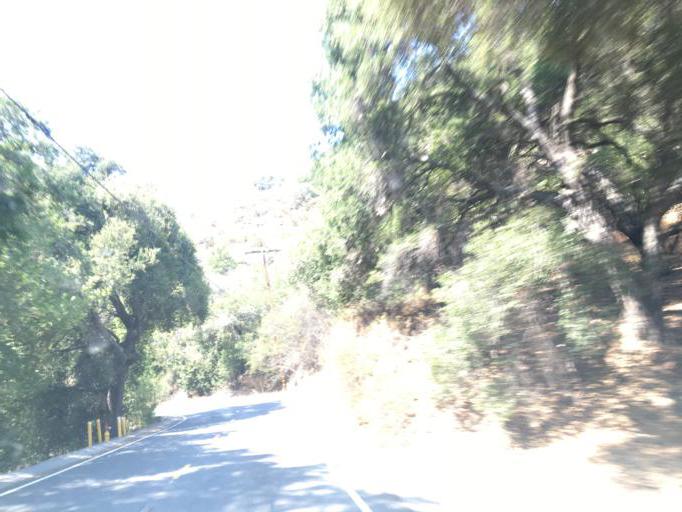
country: US
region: California
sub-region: Los Angeles County
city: Topanga
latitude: 34.0740
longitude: -118.6080
